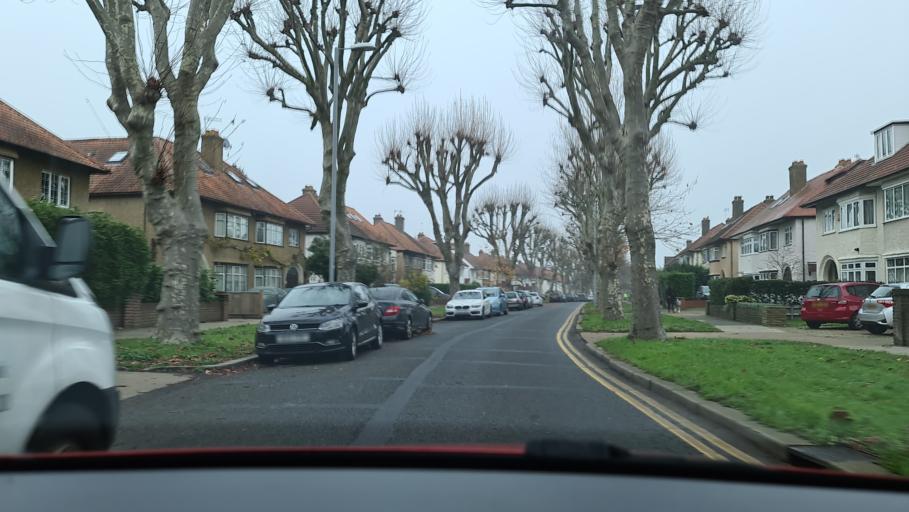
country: GB
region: England
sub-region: Greater London
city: Surbiton
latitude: 51.3834
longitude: -0.2852
